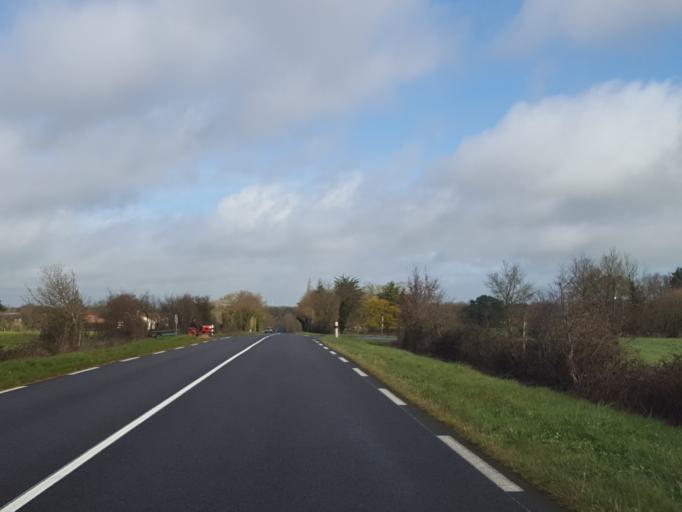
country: FR
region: Pays de la Loire
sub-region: Departement de la Vendee
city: Les Lucs-sur-Boulogne
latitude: 46.8561
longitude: -1.4967
